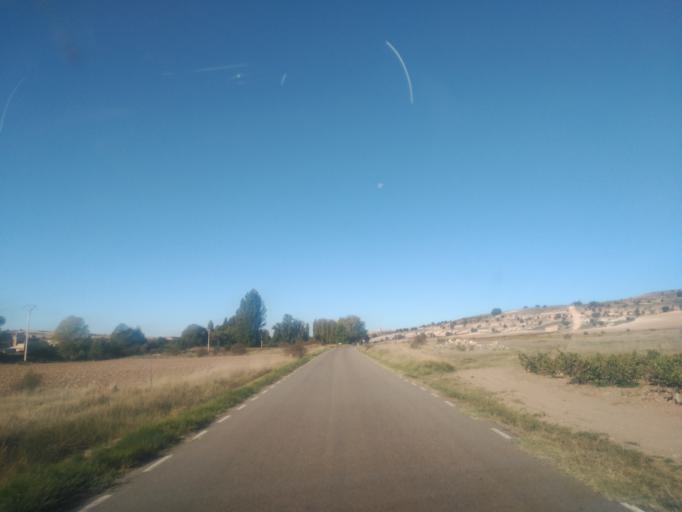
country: ES
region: Castille and Leon
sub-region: Provincia de Burgos
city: Penaranda de Duero
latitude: 41.6868
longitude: -3.4450
